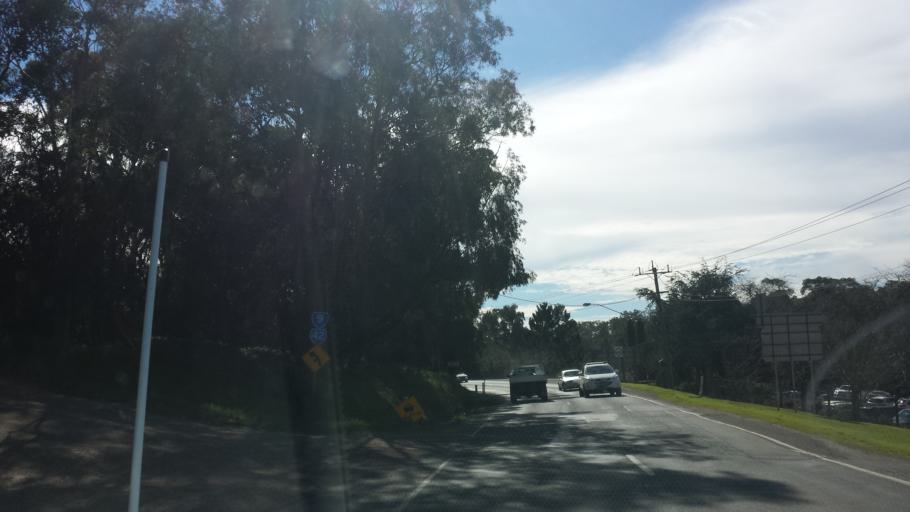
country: AU
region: Victoria
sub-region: Manningham
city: Warrandyte
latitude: -37.7458
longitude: 145.2352
